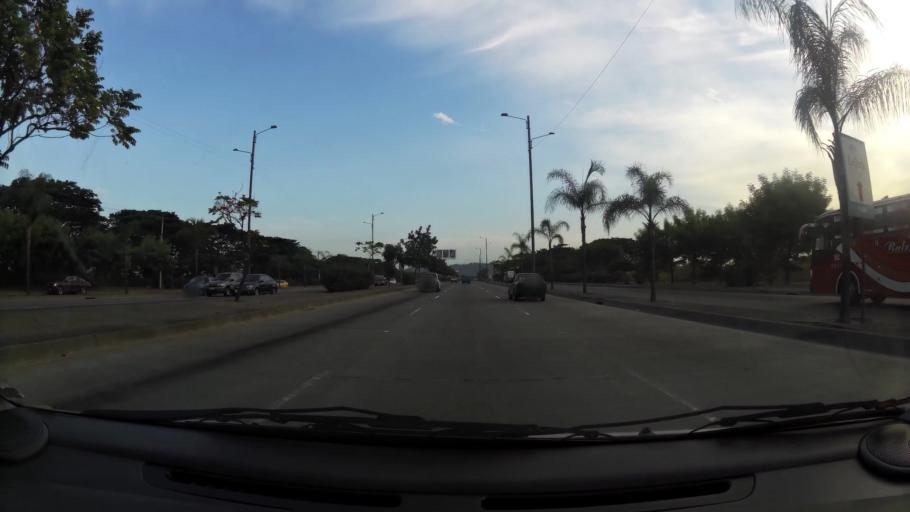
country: EC
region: Guayas
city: Eloy Alfaro
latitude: -2.0950
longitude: -79.8929
